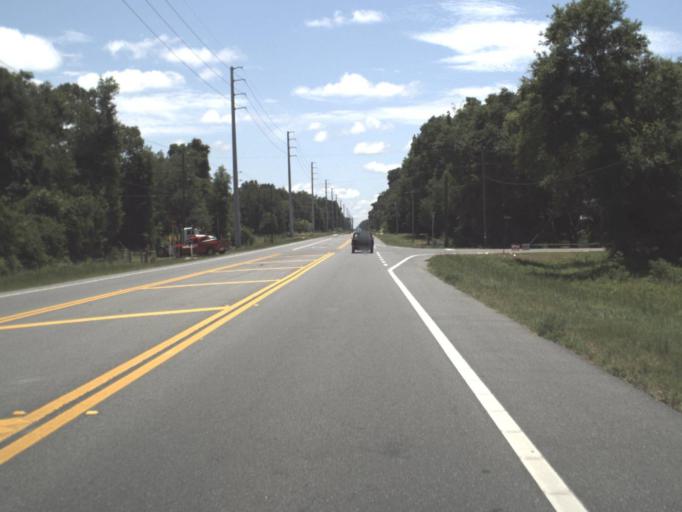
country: US
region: Florida
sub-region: Dixie County
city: Cross City
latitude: 29.6788
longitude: -82.9843
